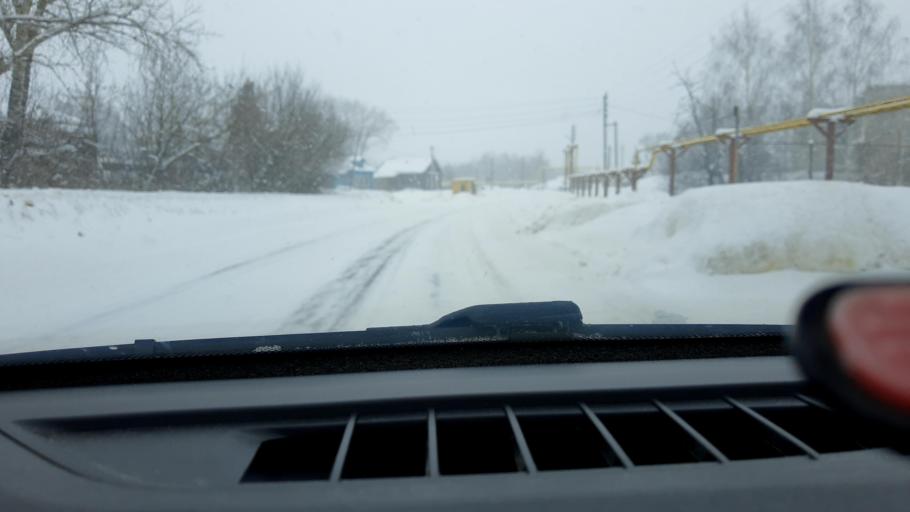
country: RU
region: Nizjnij Novgorod
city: Bol'shoye Murashkino
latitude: 55.7080
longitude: 44.7932
